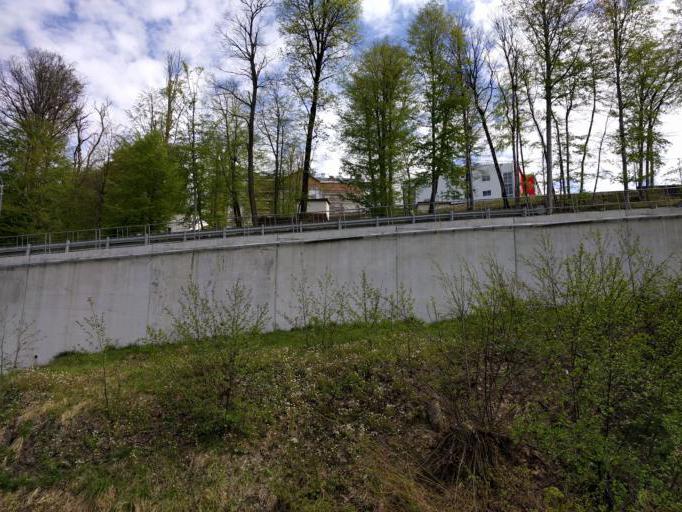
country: RU
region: Krasnodarskiy
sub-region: Sochi City
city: Krasnaya Polyana
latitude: 43.6624
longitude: 40.3130
